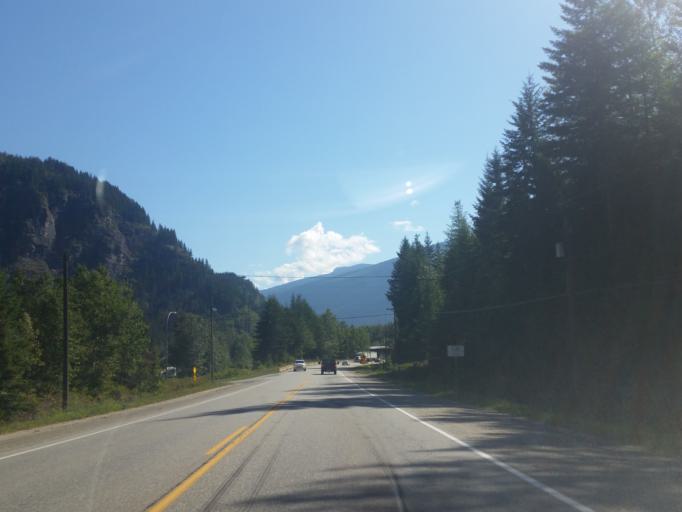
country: CA
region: British Columbia
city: Sicamous
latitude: 50.8912
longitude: -118.8698
